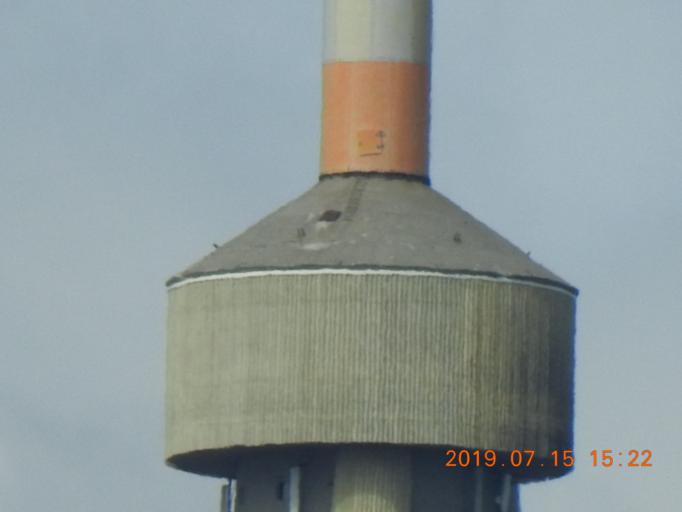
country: NO
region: Hordaland
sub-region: Voss
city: Voss
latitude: 60.6461
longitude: 6.4025
